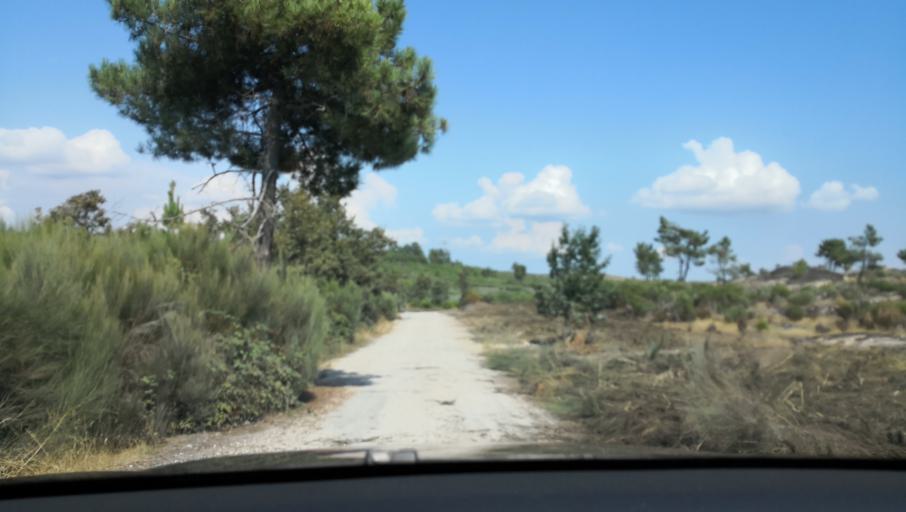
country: PT
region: Vila Real
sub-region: Sabrosa
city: Sabrosa
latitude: 41.3187
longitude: -7.6202
